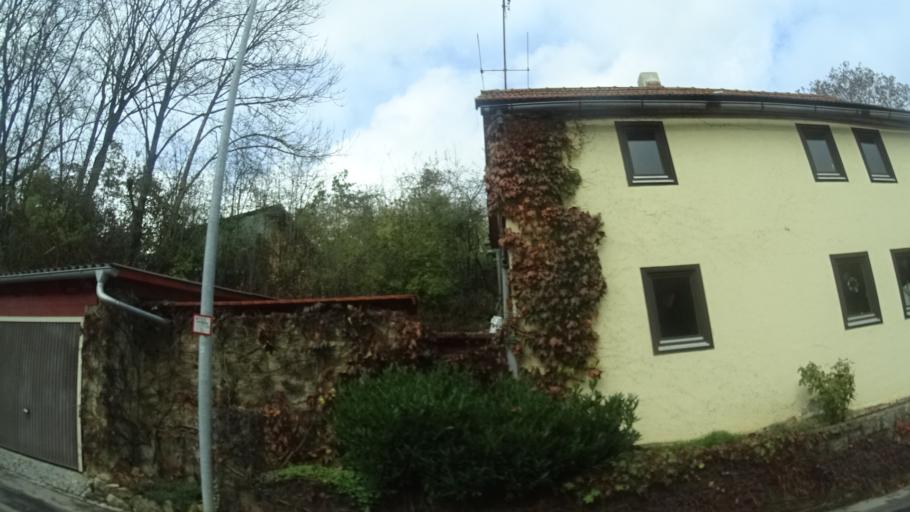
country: DE
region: Bavaria
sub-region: Regierungsbezirk Unterfranken
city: Saal an der Saale
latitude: 50.3393
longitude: 10.3849
